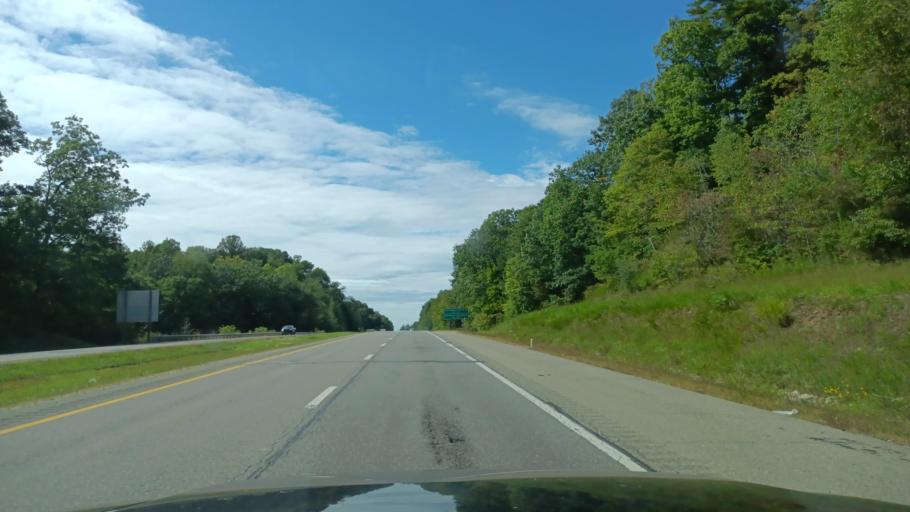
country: US
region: West Virginia
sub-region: Ritchie County
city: Pennsboro
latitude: 39.2742
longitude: -80.9990
